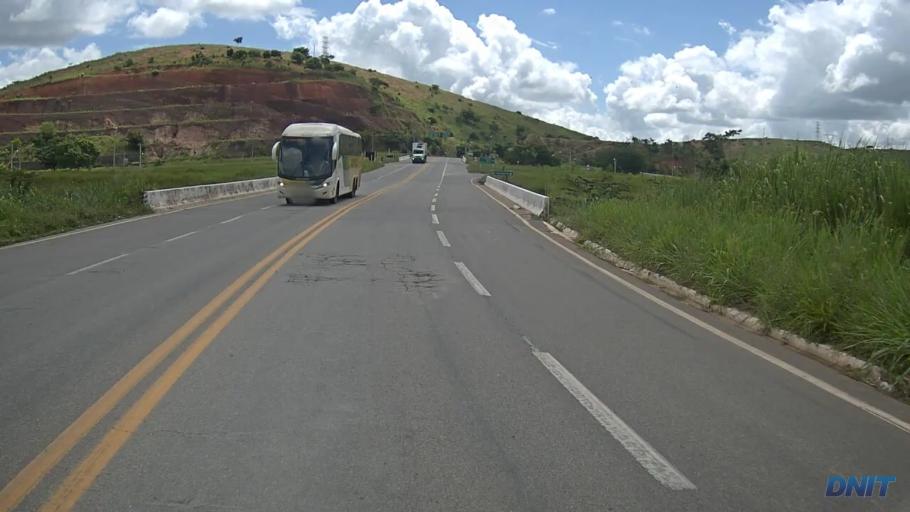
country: BR
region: Minas Gerais
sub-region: Governador Valadares
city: Governador Valadares
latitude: -18.8597
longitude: -41.9852
